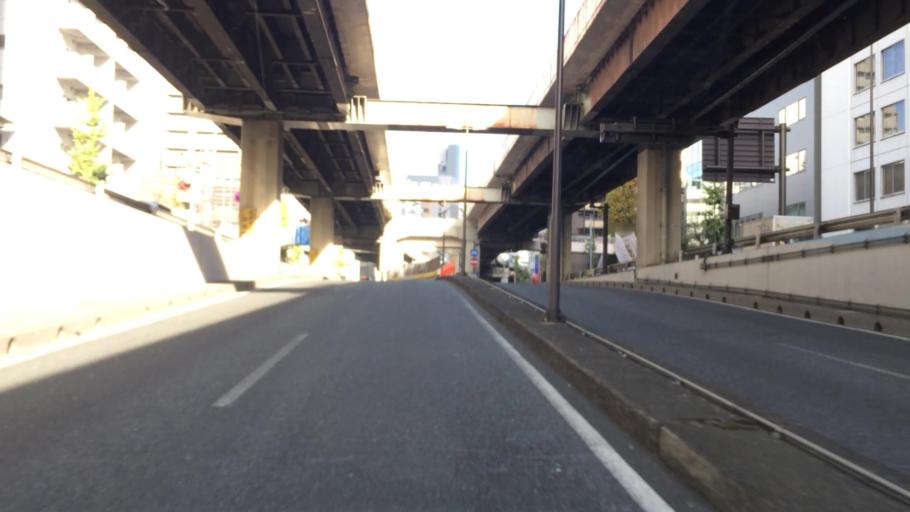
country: JP
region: Tokyo
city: Tokyo
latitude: 35.6899
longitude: 139.7754
